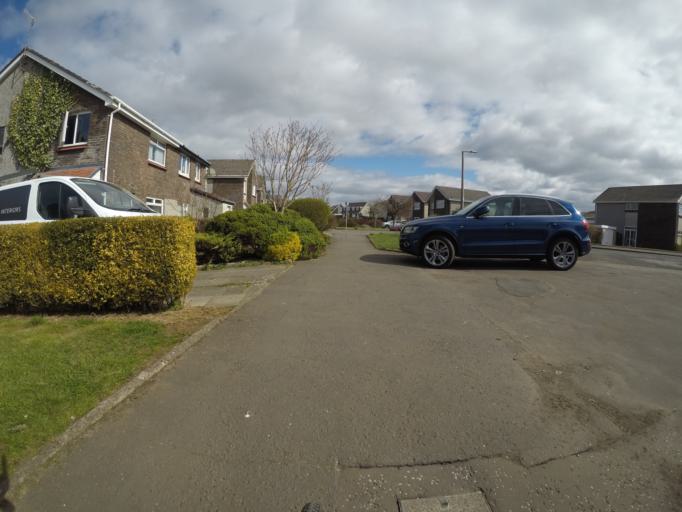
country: GB
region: Scotland
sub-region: South Ayrshire
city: Troon
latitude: 55.5664
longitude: -4.6421
